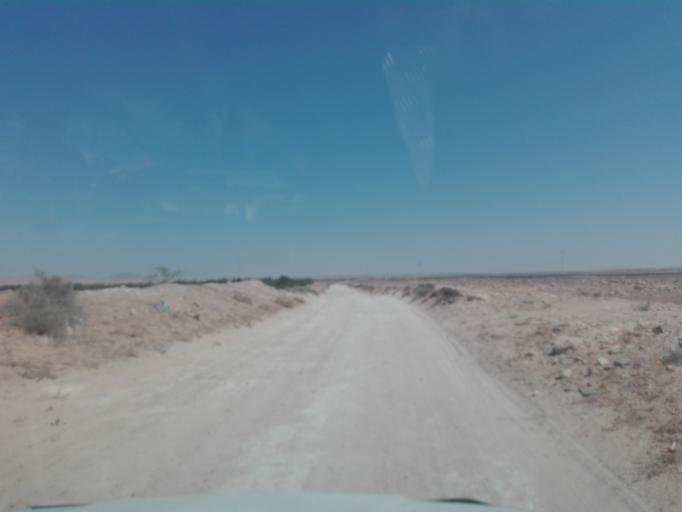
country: TN
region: Safaqis
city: Skhira
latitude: 34.3711
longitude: 9.9068
